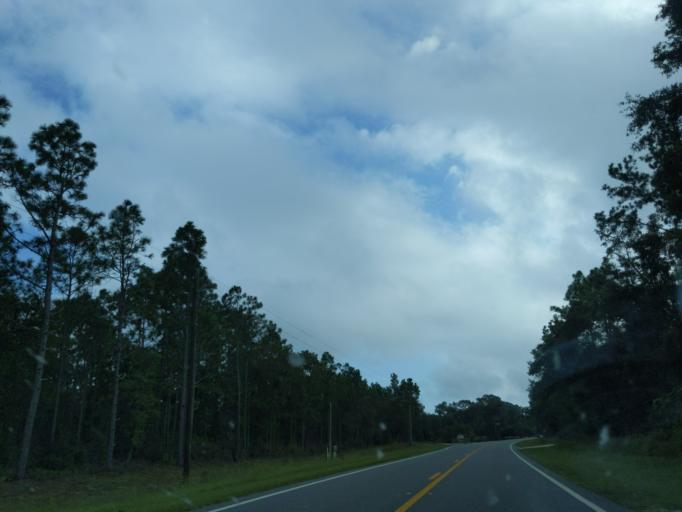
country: US
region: Florida
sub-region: Wakulla County
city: Crawfordville
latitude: 30.1229
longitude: -84.3151
